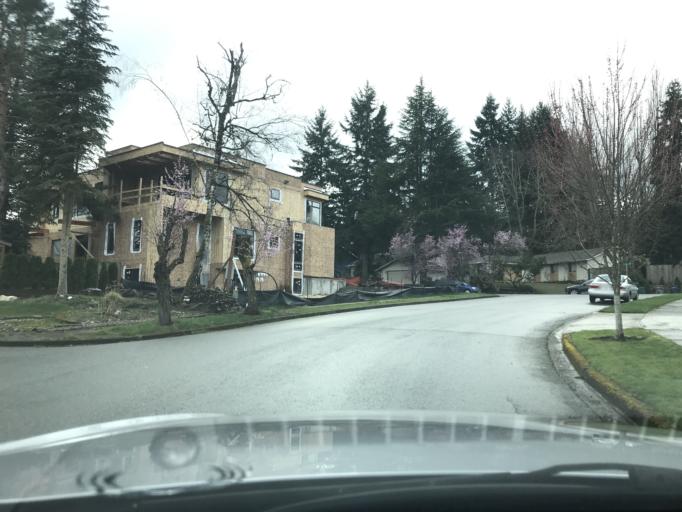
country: US
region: Washington
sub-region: King County
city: Redmond
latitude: 47.6565
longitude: -122.1279
